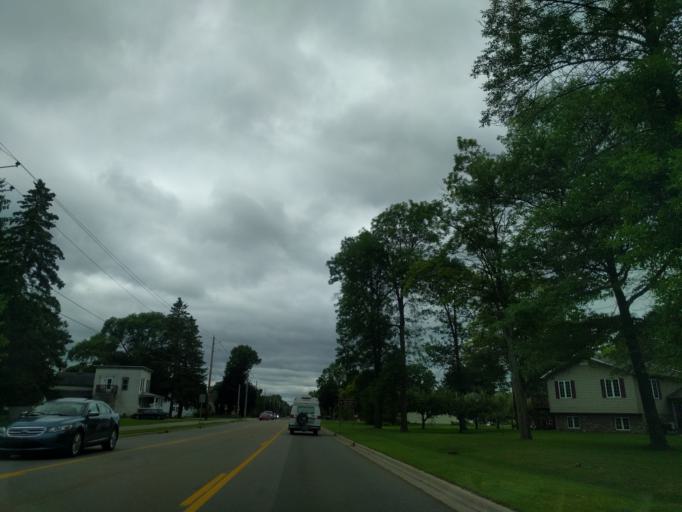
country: US
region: Michigan
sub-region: Menominee County
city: Menominee
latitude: 45.1391
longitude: -87.6051
